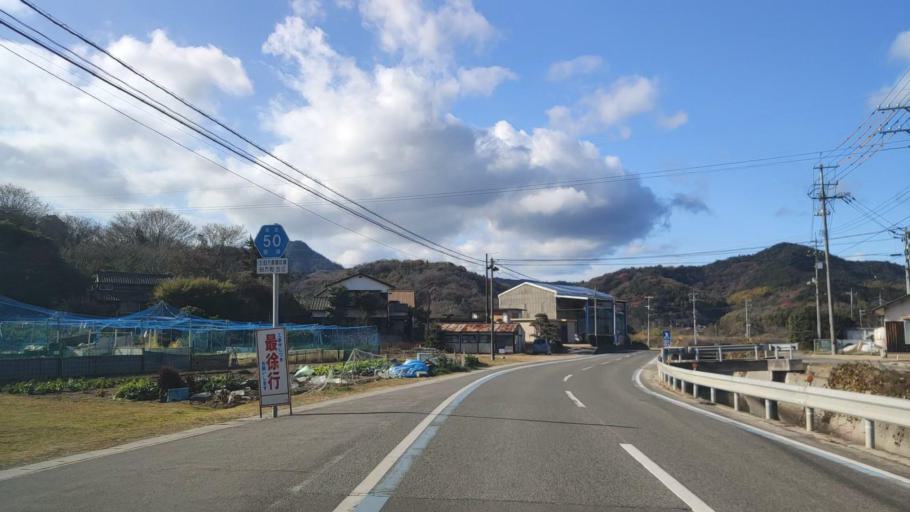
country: JP
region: Hiroshima
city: Innoshima
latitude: 34.2131
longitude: 133.1109
